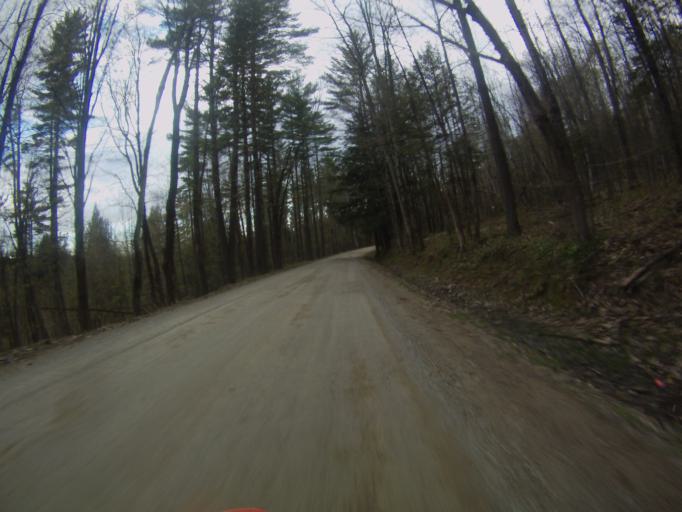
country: US
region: Vermont
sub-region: Addison County
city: Middlebury (village)
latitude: 43.9818
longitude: -73.0560
